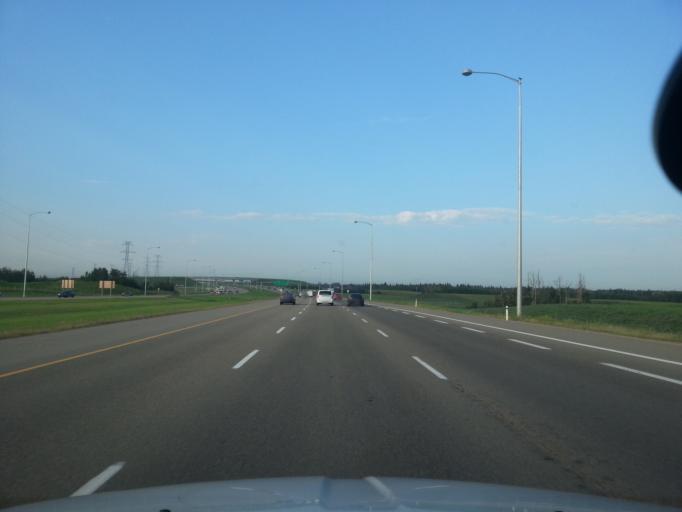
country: CA
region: Alberta
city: St. Albert
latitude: 53.5855
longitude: -113.6548
